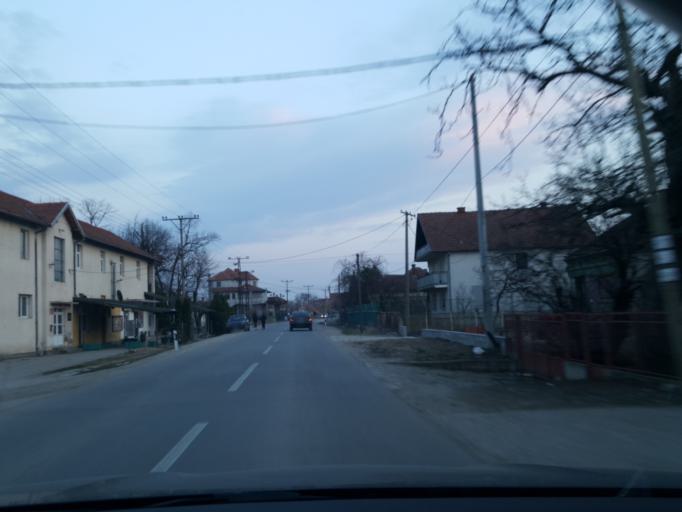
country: RS
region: Central Serbia
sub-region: Nisavski Okrug
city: Aleksinac
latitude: 43.5012
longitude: 21.7026
